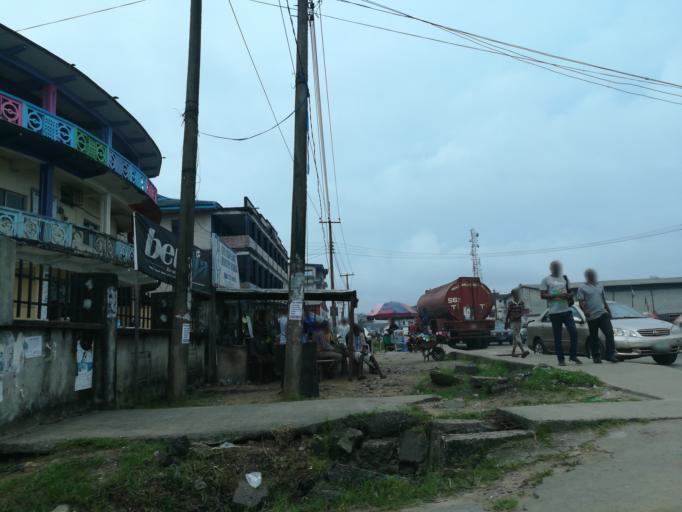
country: NG
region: Rivers
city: Port Harcourt
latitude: 4.7626
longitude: 7.0137
